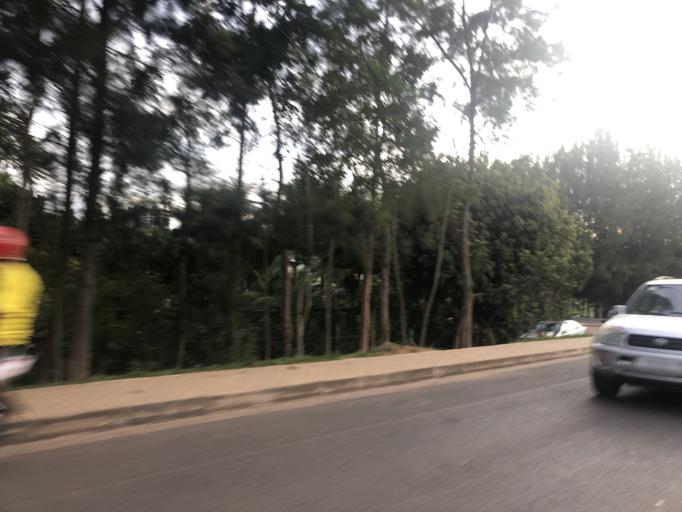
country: RW
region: Kigali
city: Kigali
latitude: -1.9318
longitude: 30.0864
